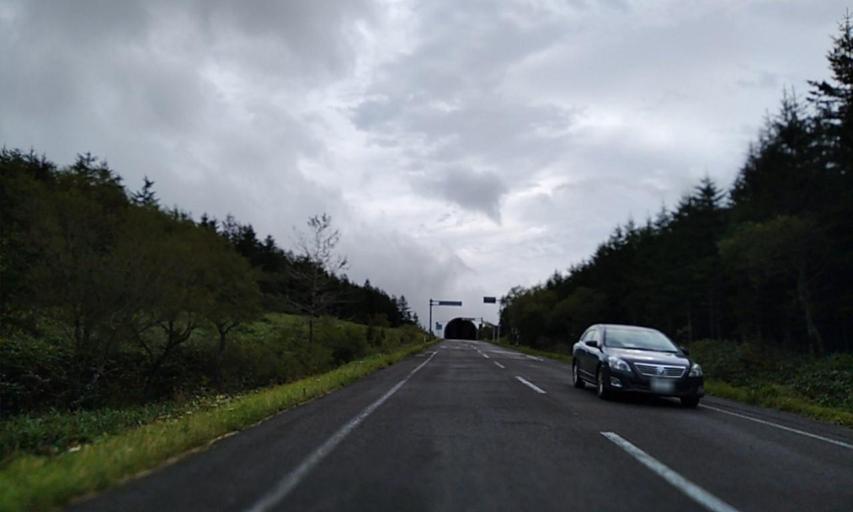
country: JP
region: Hokkaido
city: Abashiri
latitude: 43.6139
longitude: 144.5894
